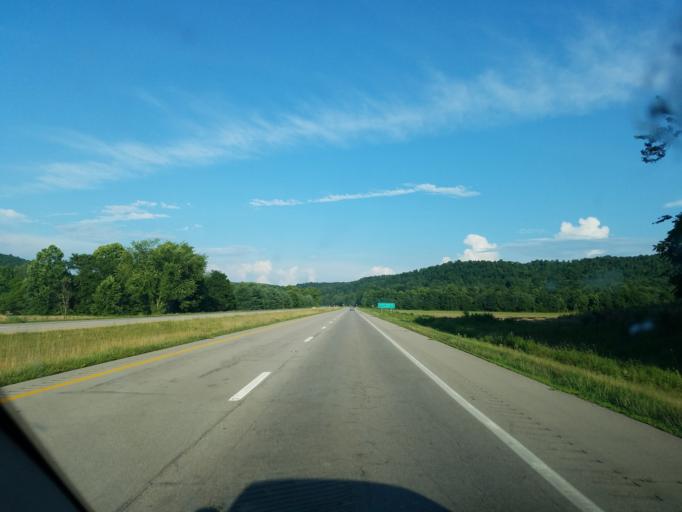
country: US
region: Ohio
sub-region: Pike County
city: Piketon
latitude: 39.0455
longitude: -83.1751
